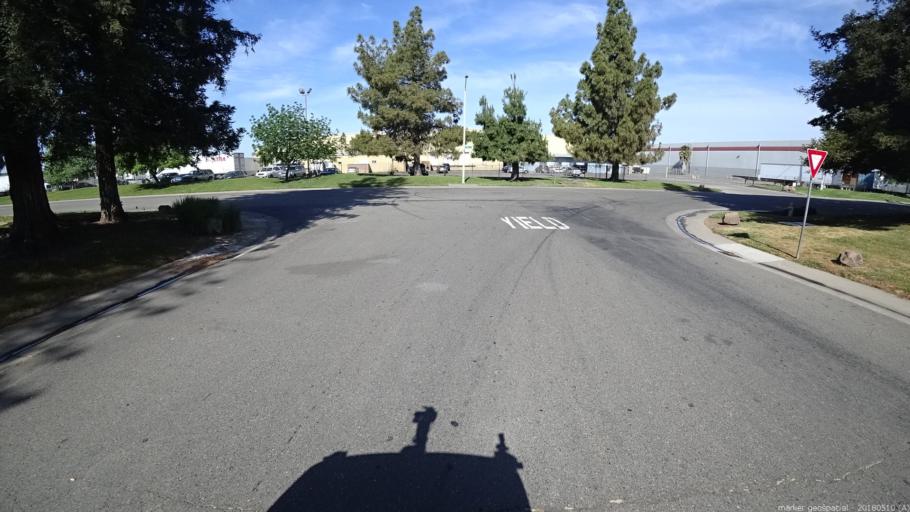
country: US
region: California
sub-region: Sacramento County
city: Rio Linda
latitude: 38.6449
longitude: -121.4698
